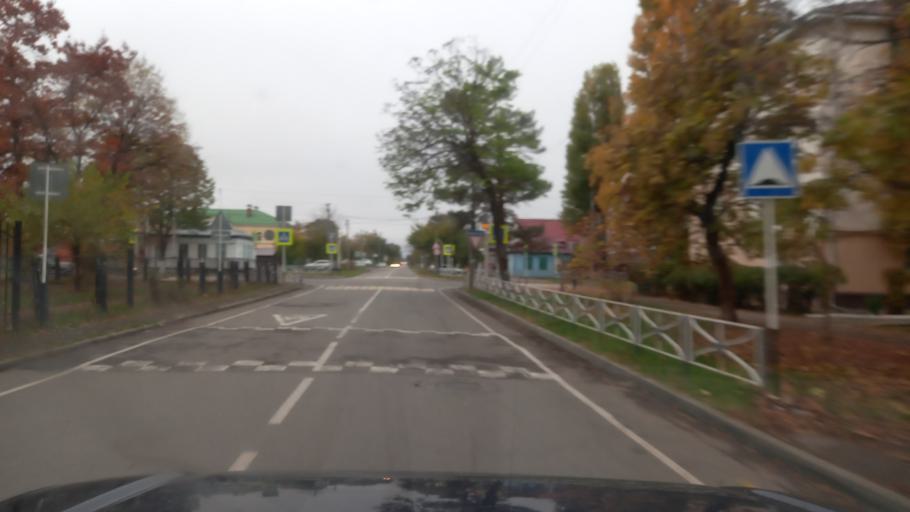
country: RU
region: Adygeya
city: Maykop
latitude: 44.6159
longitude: 40.1050
